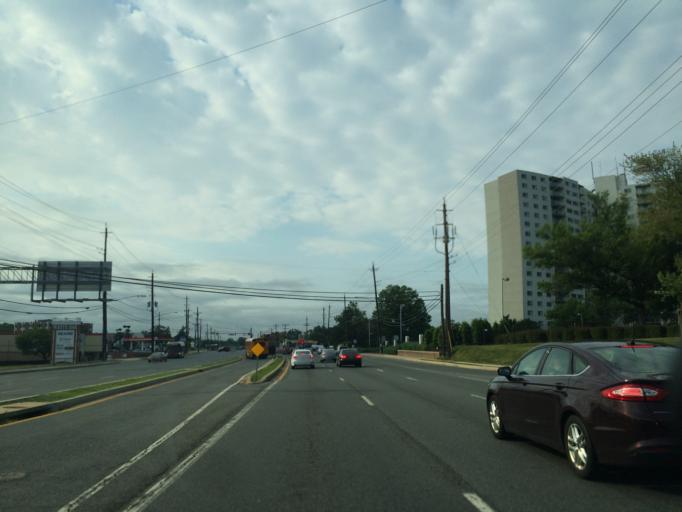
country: US
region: Maryland
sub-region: Montgomery County
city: White Oak
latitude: 39.0418
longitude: -76.9916
